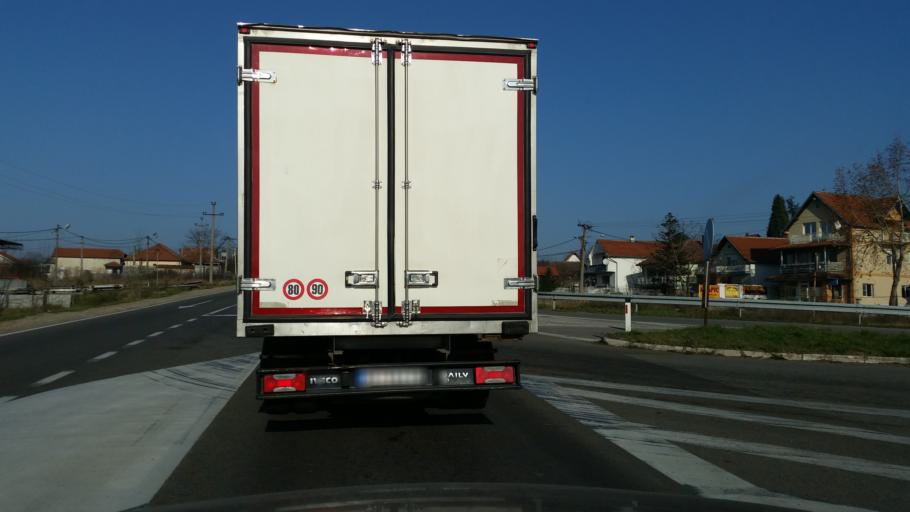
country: RS
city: Stepojevac
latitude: 44.5051
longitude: 20.2922
